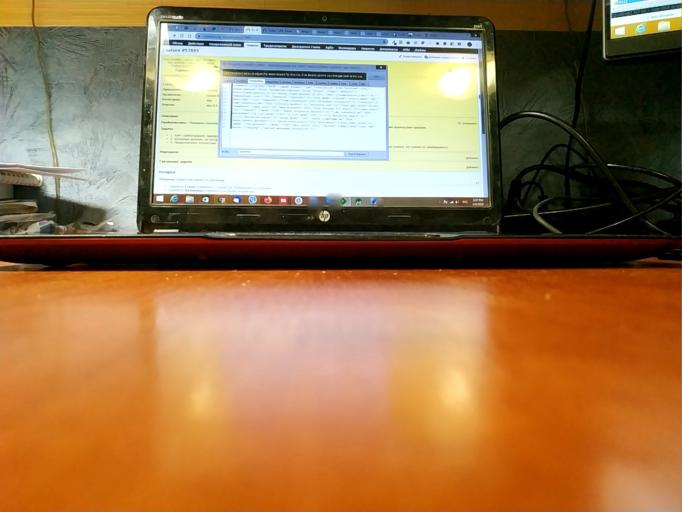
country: RU
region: Tverskaya
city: Sandovo
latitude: 58.5655
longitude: 36.4019
